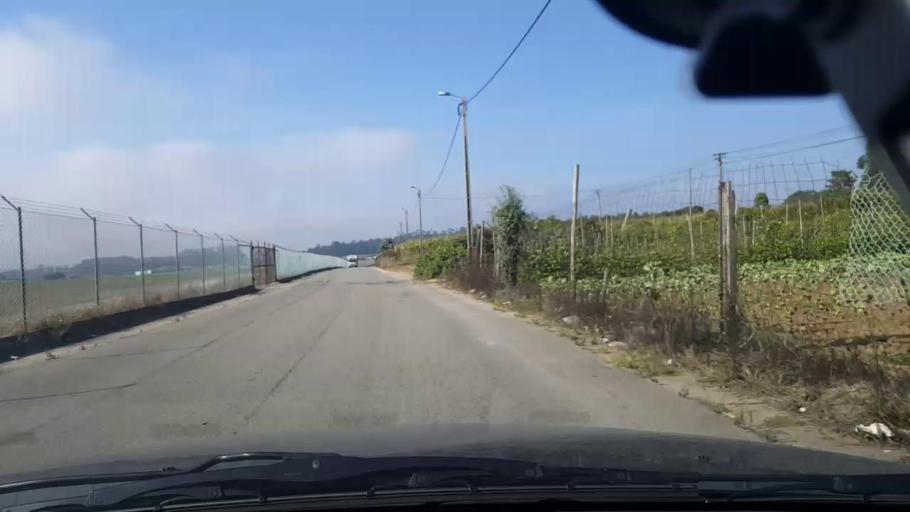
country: PT
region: Porto
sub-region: Matosinhos
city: Lavra
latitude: 41.2631
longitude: -8.6829
